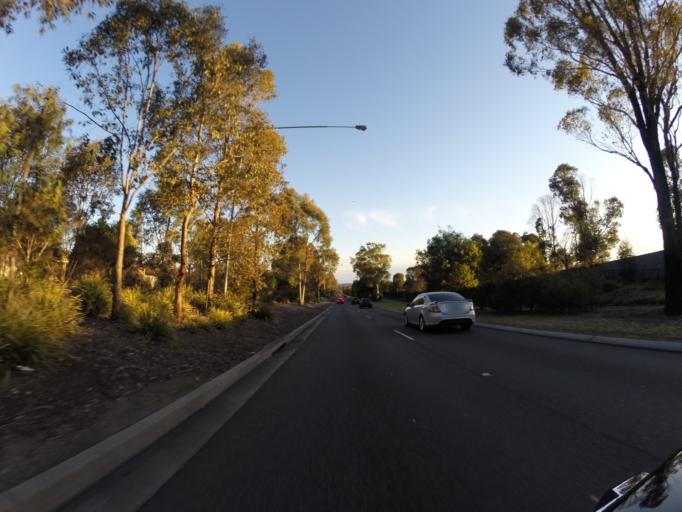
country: AU
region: New South Wales
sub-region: Fairfield
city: Cecil Park
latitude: -33.8903
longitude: 150.8601
